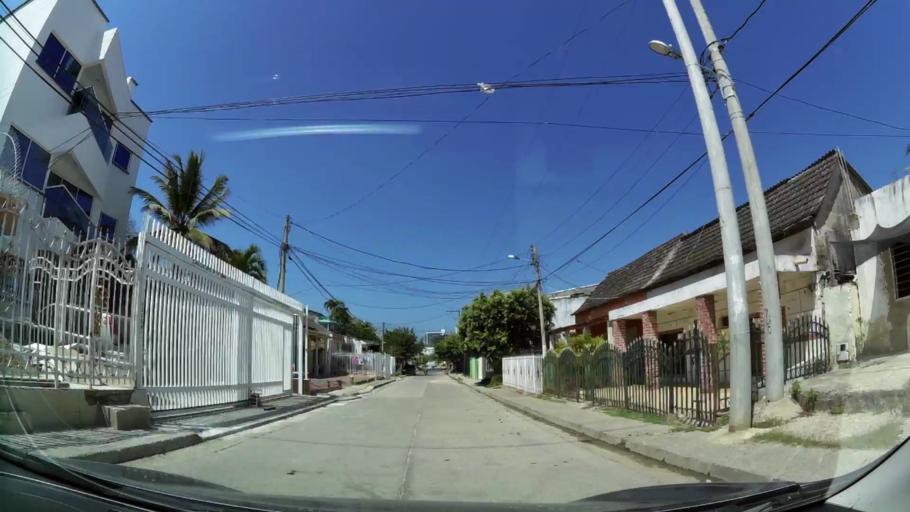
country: CO
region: Bolivar
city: Cartagena
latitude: 10.4297
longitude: -75.5326
